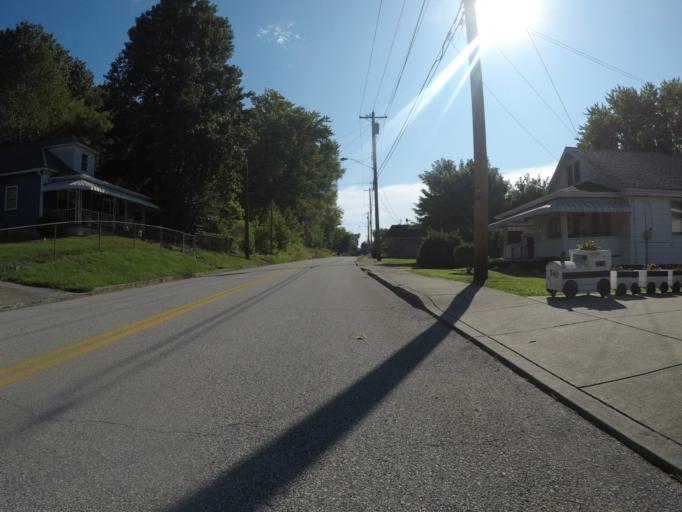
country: US
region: Kentucky
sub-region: Boyd County
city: Ashland
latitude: 38.4549
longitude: -82.6215
